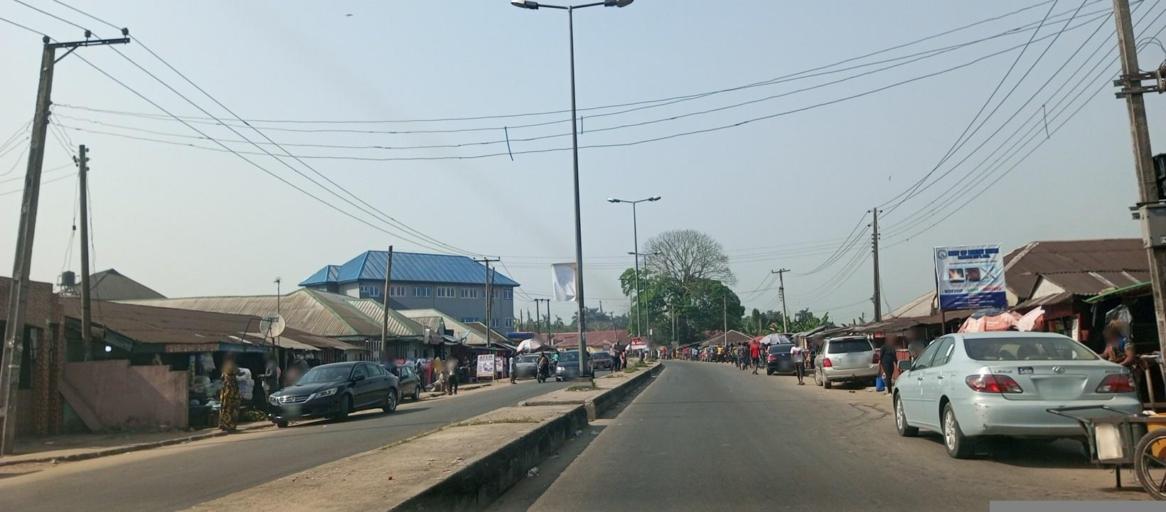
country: NG
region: Rivers
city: Emuoha
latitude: 4.8893
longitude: 6.9019
